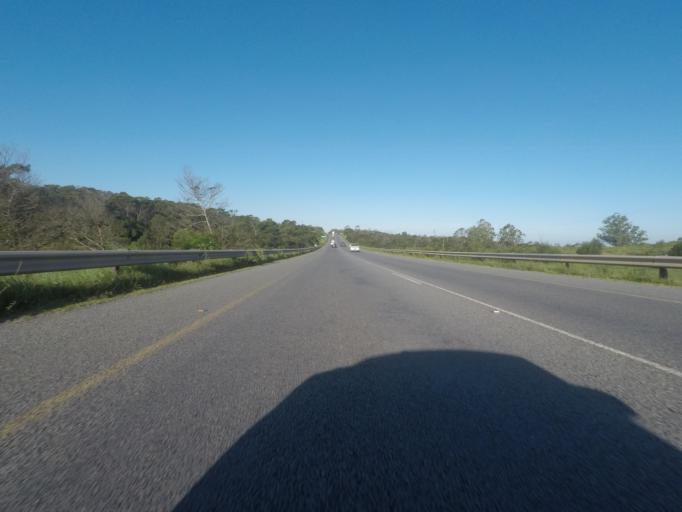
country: ZA
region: Eastern Cape
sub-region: Buffalo City Metropolitan Municipality
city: East London
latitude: -33.0509
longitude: 27.8124
